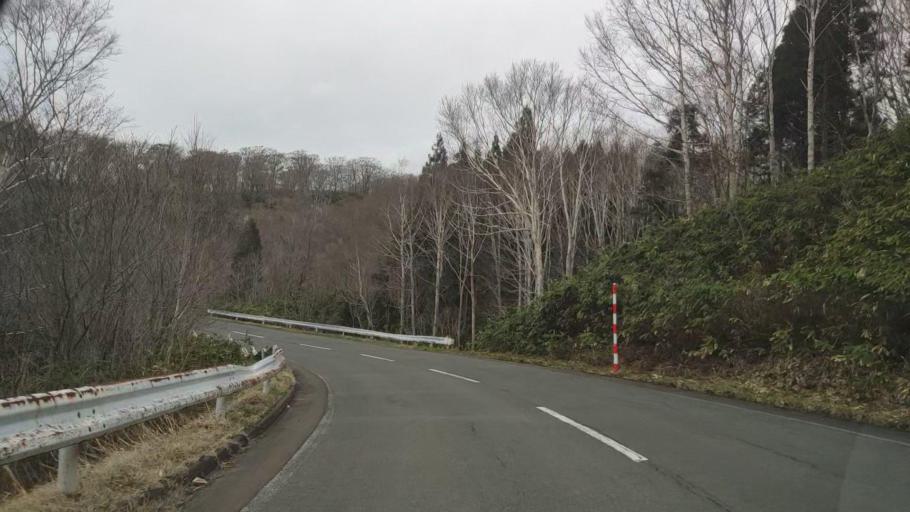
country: JP
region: Akita
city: Hanawa
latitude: 40.4175
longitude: 140.8405
